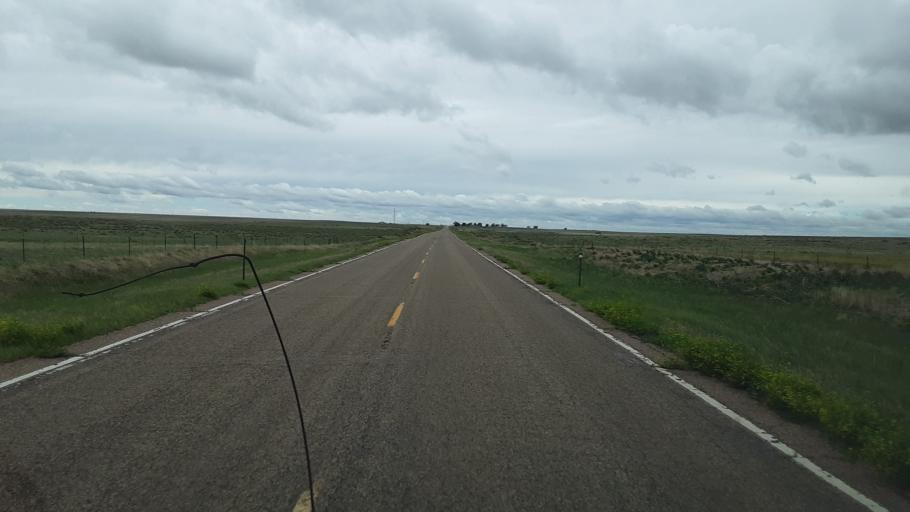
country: US
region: Colorado
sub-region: Lincoln County
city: Hugo
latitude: 38.8518
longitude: -103.6803
